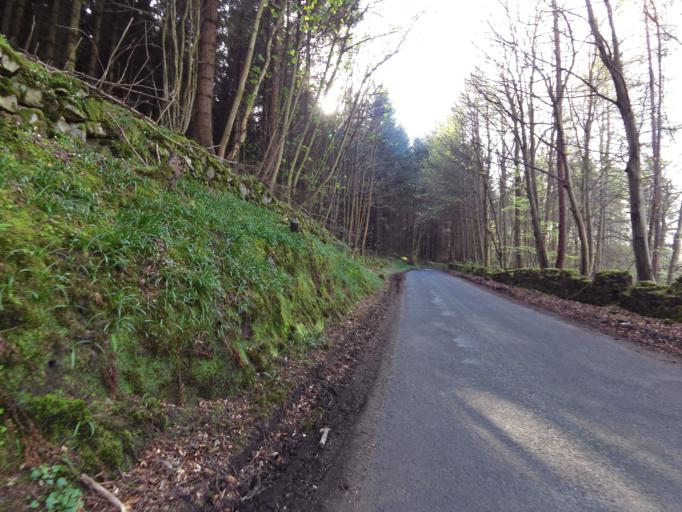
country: GB
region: Scotland
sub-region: Fife
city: Falkland
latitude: 56.2500
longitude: -3.2189
